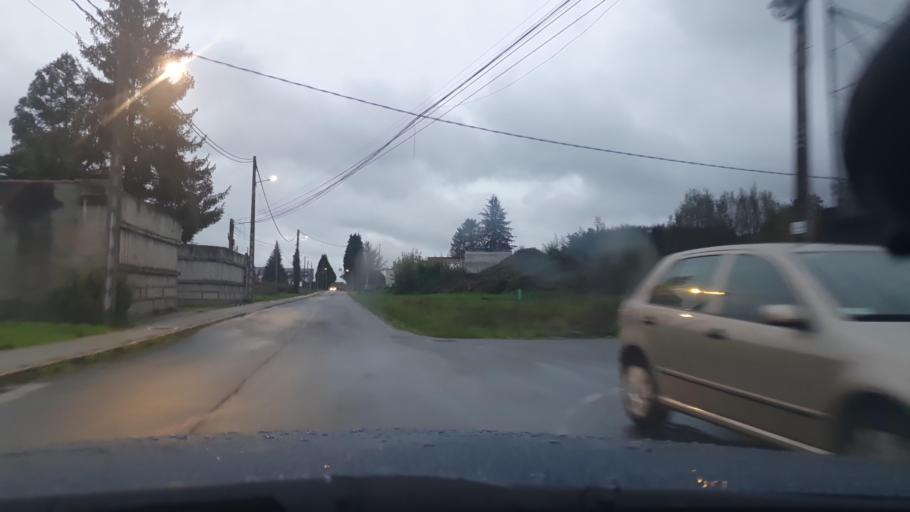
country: ES
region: Galicia
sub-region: Provincia da Coruna
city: Santiago de Compostela
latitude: 42.8506
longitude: -8.5887
